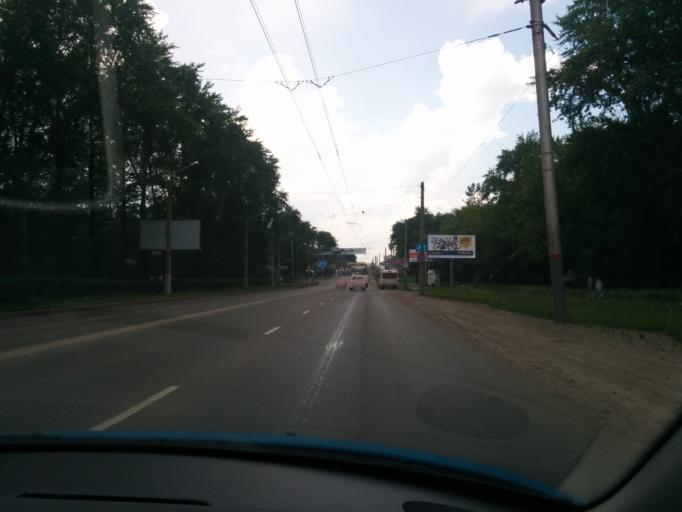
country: RU
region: Perm
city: Kondratovo
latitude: 57.9776
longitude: 56.1675
